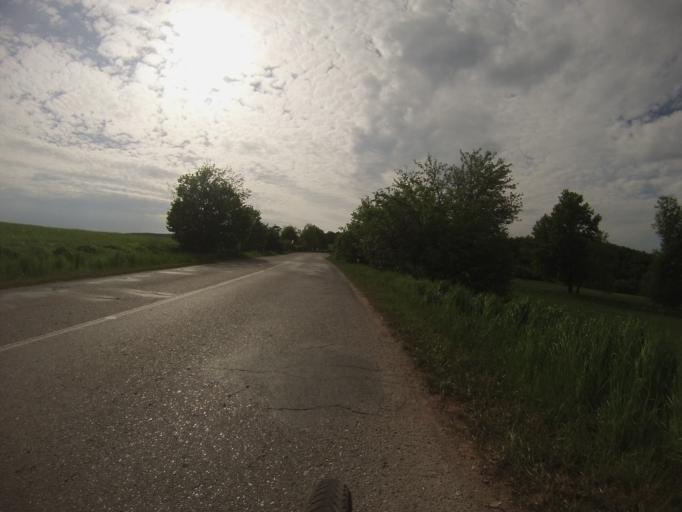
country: CZ
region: South Moravian
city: Veverska Bityska
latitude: 49.2542
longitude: 16.4540
